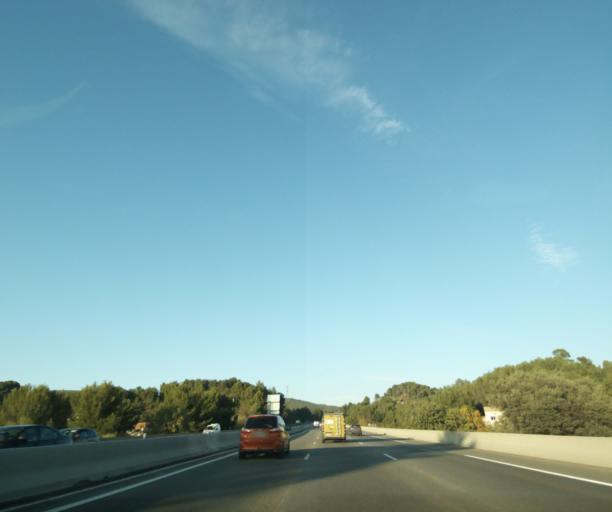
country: FR
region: Provence-Alpes-Cote d'Azur
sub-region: Departement des Bouches-du-Rhone
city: Roquevaire
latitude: 43.3377
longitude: 5.6079
